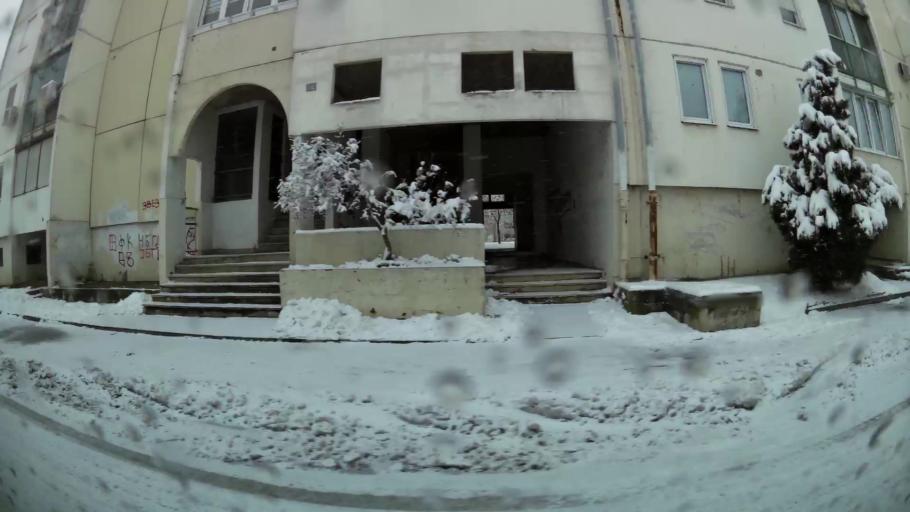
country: RS
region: Central Serbia
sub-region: Belgrade
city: Cukarica
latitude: 44.7927
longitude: 20.3721
